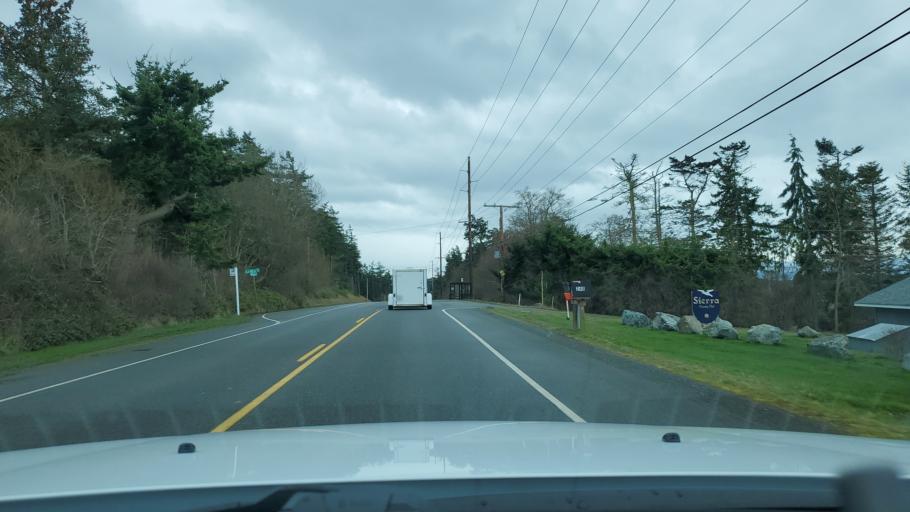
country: US
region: Washington
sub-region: Island County
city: Coupeville
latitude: 48.2392
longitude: -122.7517
